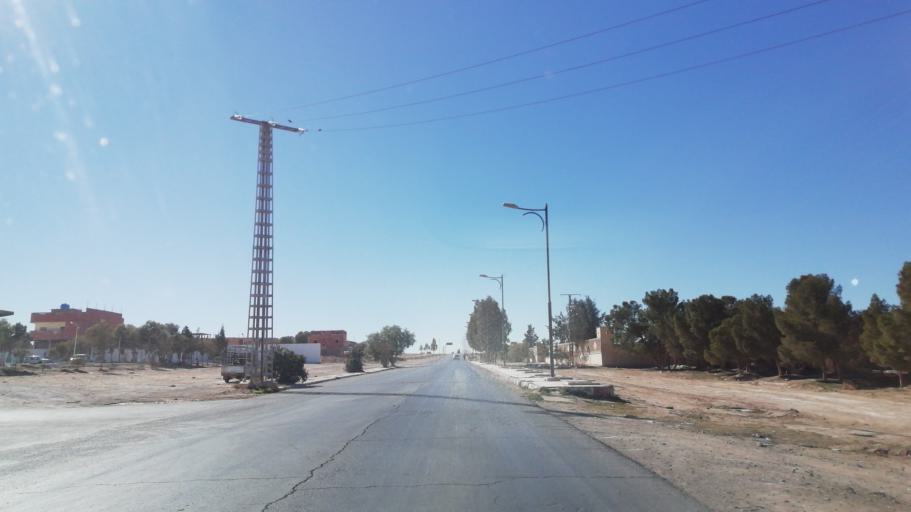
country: DZ
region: Saida
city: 'Ain el Hadjar
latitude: 34.0389
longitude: 0.0801
